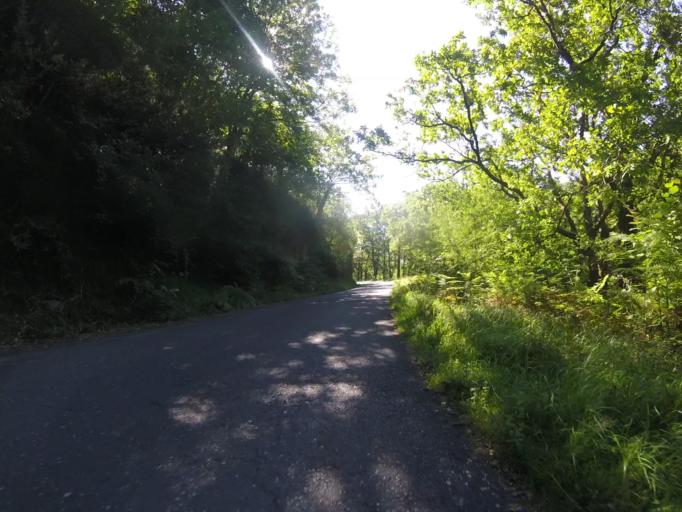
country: ES
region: Navarre
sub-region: Provincia de Navarra
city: Goizueta
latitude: 43.1894
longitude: -1.8463
